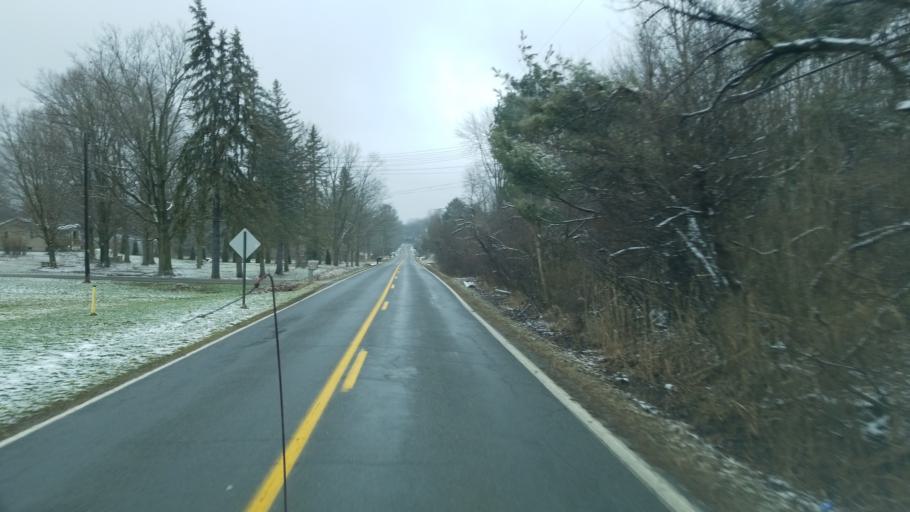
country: US
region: Ohio
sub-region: Portage County
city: Aurora
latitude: 41.2842
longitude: -81.2894
